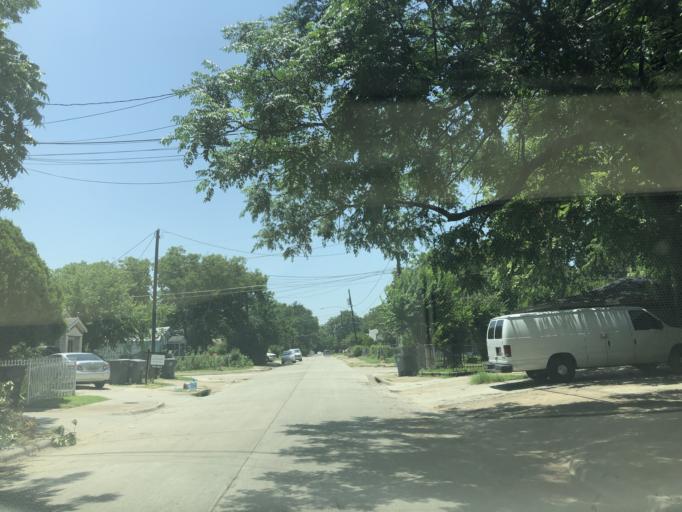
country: US
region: Texas
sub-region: Dallas County
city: Dallas
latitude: 32.7750
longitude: -96.8382
